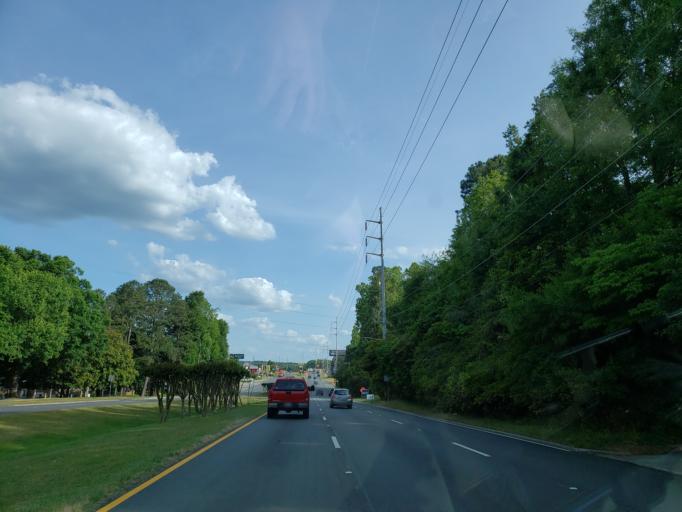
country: US
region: Georgia
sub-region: Carroll County
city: Carrollton
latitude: 33.5721
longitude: -85.0789
